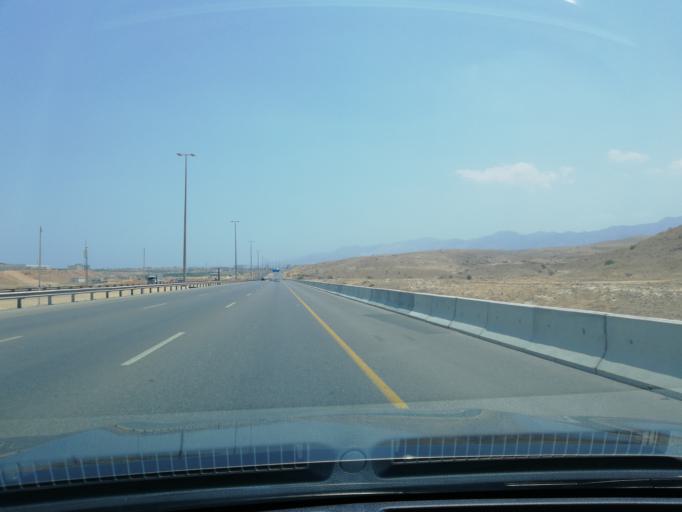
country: OM
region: Muhafazat Masqat
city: Bawshar
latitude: 23.5565
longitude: 58.3106
